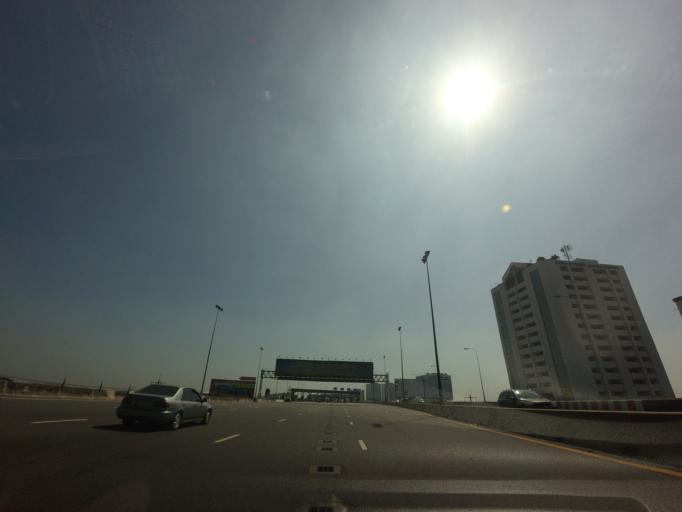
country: TH
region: Bangkok
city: Bang Na
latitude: 13.6609
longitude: 100.6620
